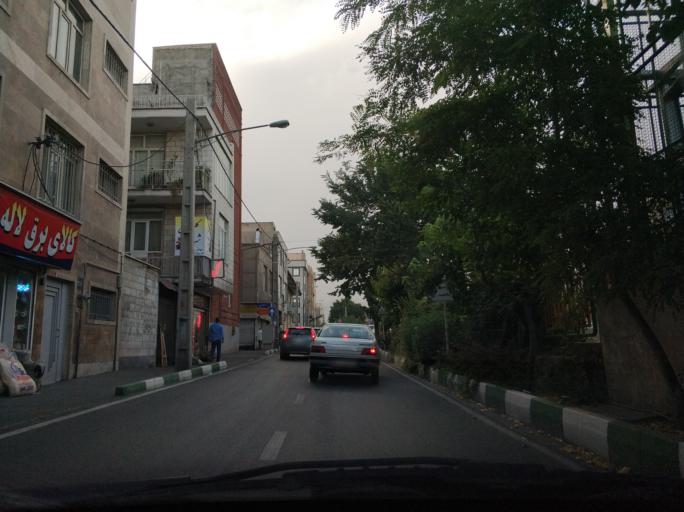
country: IR
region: Tehran
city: Tehran
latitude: 35.7151
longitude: 51.4822
